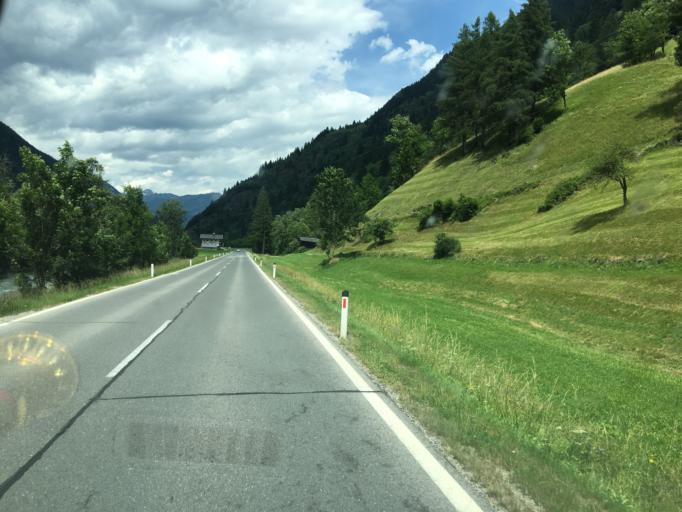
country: AT
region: Carinthia
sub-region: Politischer Bezirk Spittal an der Drau
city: Mortschach
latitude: 46.9290
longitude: 12.9062
